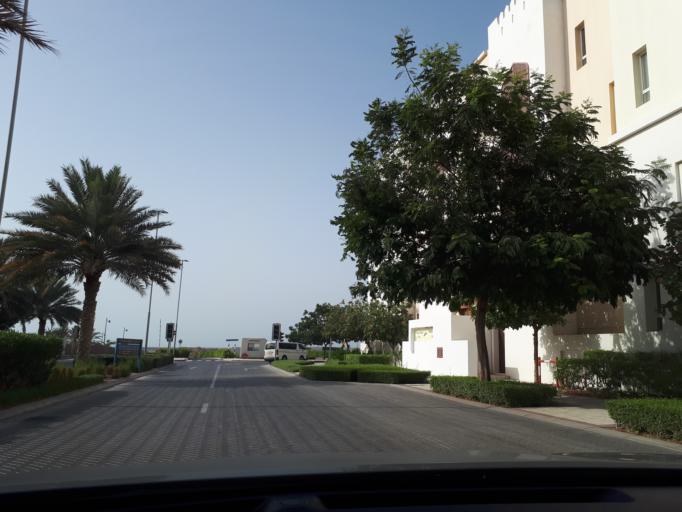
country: OM
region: Muhafazat Masqat
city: As Sib al Jadidah
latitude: 23.6294
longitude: 58.2650
